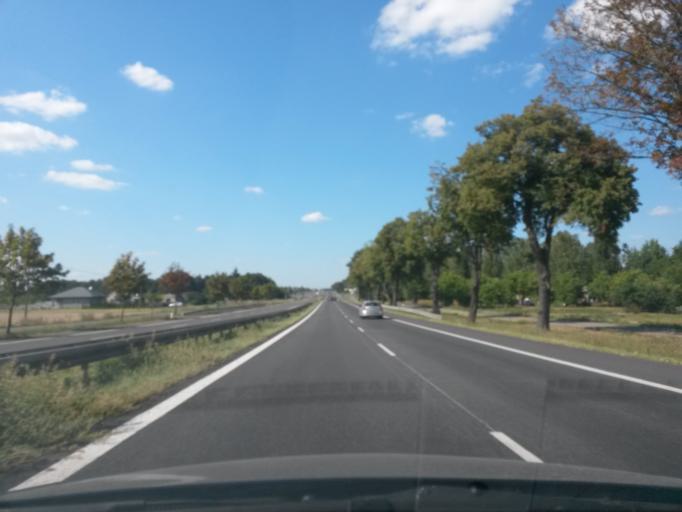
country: PL
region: Masovian Voivodeship
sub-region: Powiat plonski
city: Zaluski
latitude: 52.5625
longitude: 20.4912
